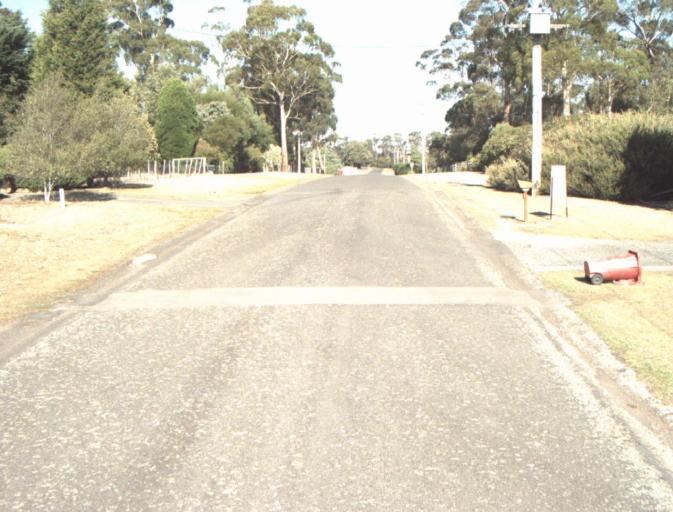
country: AU
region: Tasmania
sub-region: Launceston
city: Mayfield
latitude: -41.3249
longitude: 147.0552
